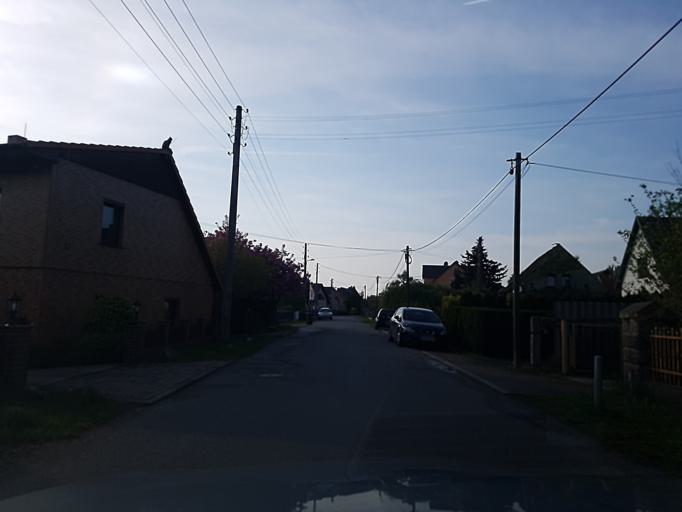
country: DE
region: Brandenburg
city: Bad Liebenwerda
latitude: 51.5162
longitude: 13.4161
